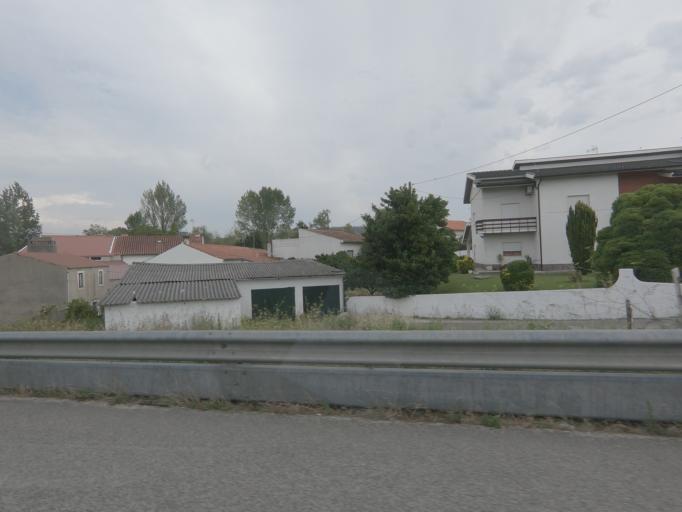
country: PT
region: Coimbra
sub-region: Condeixa-A-Nova
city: Condeixa-a-Nova
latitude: 40.1300
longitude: -8.4803
